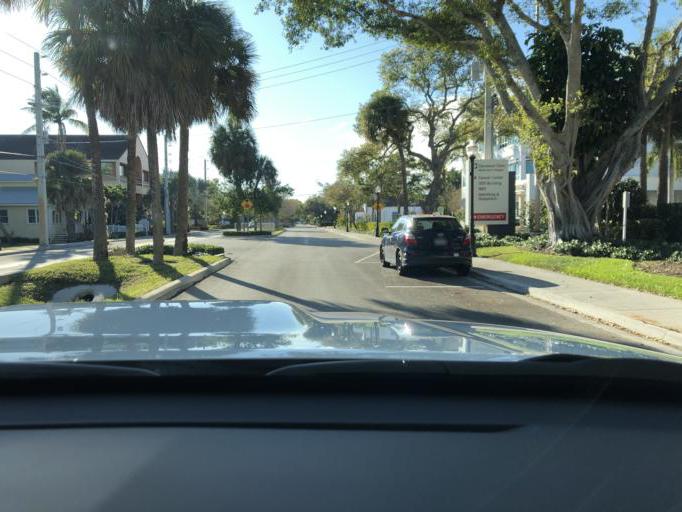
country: US
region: Florida
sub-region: Martin County
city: Stuart
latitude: 27.1984
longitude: -80.2441
